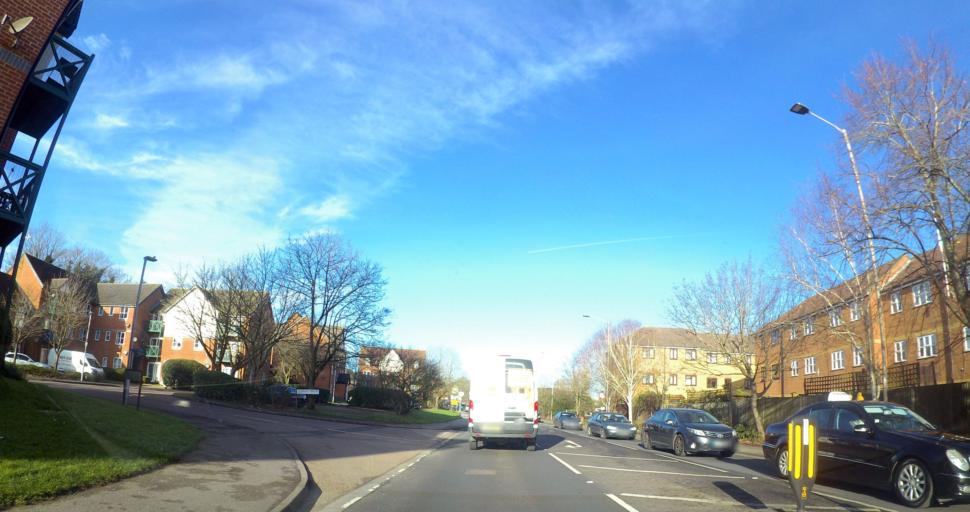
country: GB
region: England
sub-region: Reading
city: Reading
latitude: 51.4467
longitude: -0.9762
